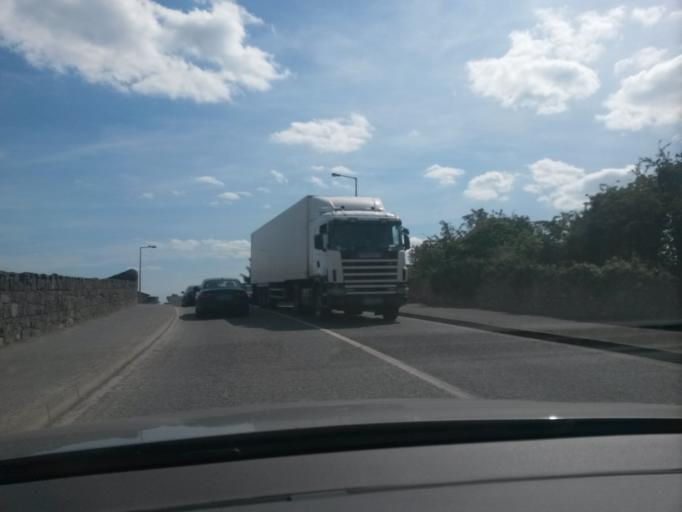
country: IE
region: Leinster
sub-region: Kildare
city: Sallins
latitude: 53.2471
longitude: -6.6656
